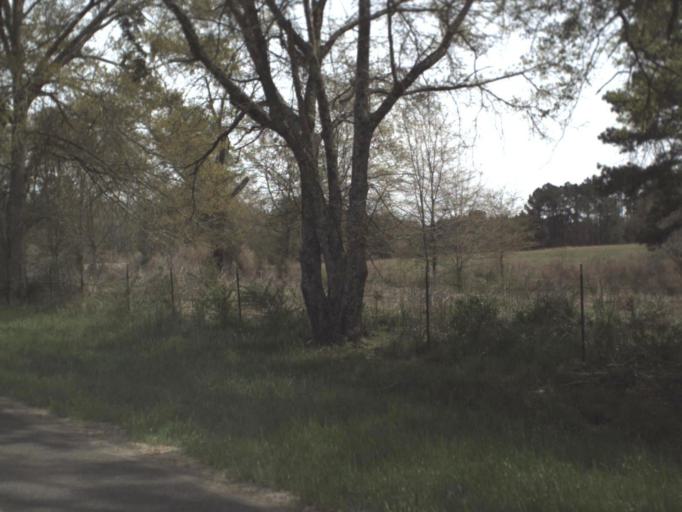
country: US
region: Alabama
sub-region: Geneva County
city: Hartford
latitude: 30.9590
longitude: -85.6850
